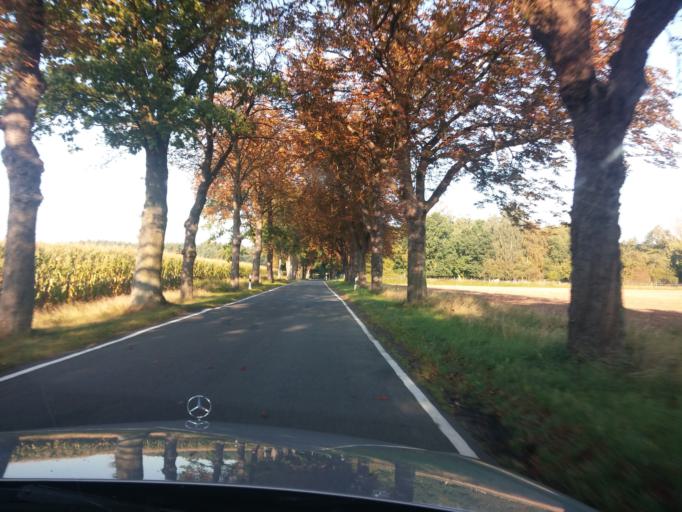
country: DE
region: Brandenburg
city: Putlitz
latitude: 53.2782
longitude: 12.0651
